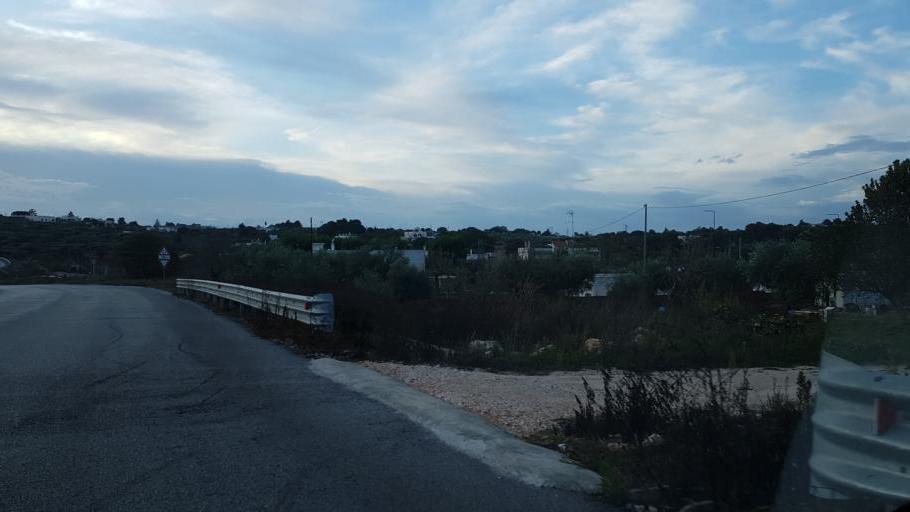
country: IT
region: Apulia
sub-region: Provincia di Bari
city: Locorotondo
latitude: 40.7645
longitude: 17.3279
